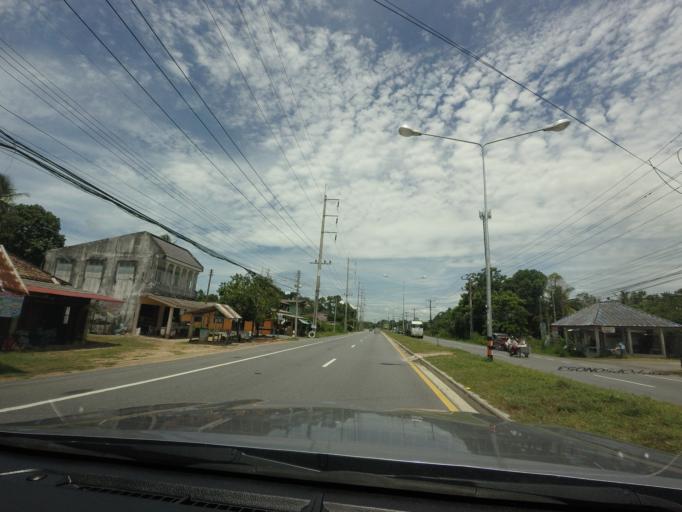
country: TH
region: Songkhla
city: Krasae Sin
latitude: 7.5732
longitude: 100.4096
